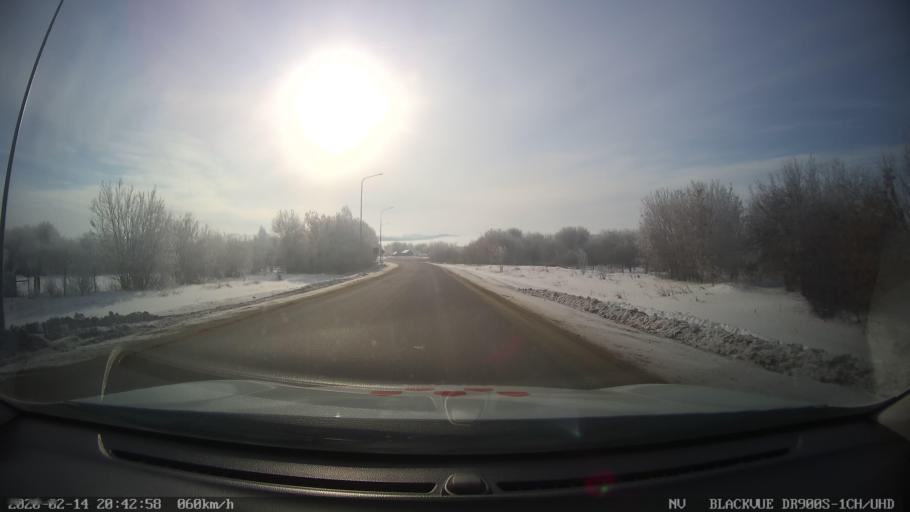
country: RU
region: Tatarstan
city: Kuybyshevskiy Zaton
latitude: 55.3128
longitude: 49.1447
